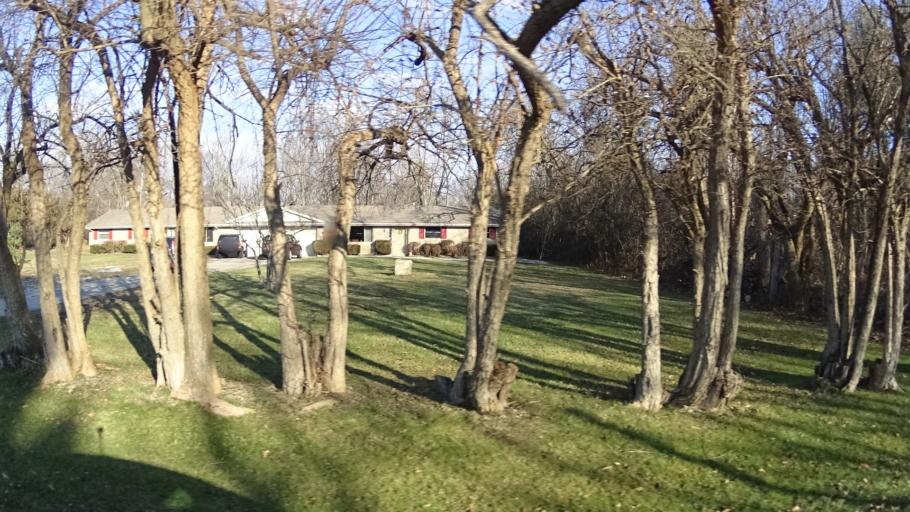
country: US
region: Ohio
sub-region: Lorain County
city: Oberlin
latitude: 41.2653
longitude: -82.1988
